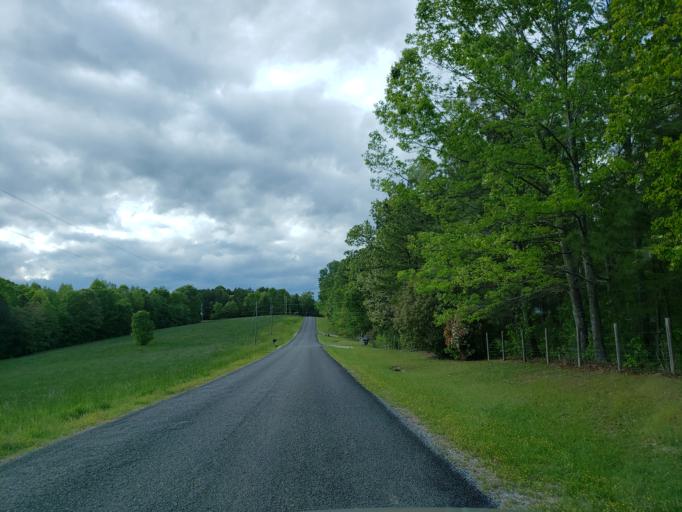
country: US
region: Georgia
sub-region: Haralson County
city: Tallapoosa
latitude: 33.8075
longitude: -85.3847
